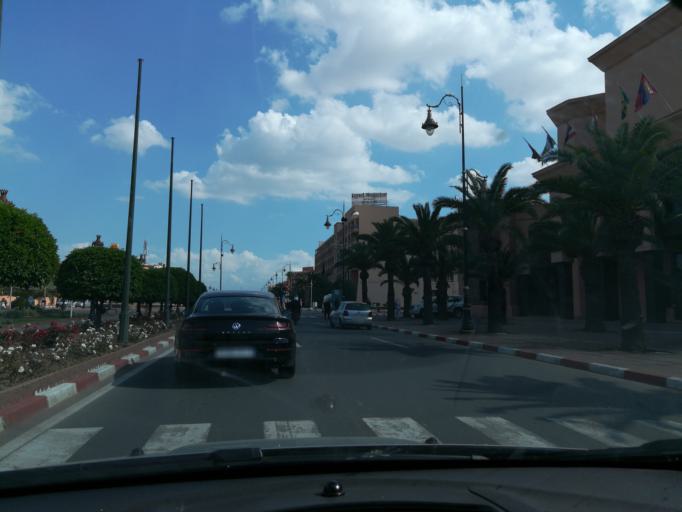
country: MA
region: Marrakech-Tensift-Al Haouz
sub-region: Marrakech
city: Marrakesh
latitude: 31.6253
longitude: -8.0131
